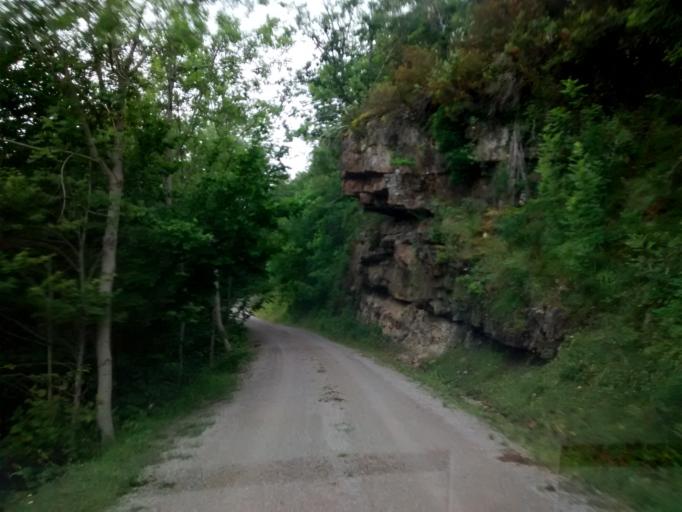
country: ES
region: La Rioja
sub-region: Provincia de La Rioja
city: Ajamil
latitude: 42.1477
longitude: -2.4798
